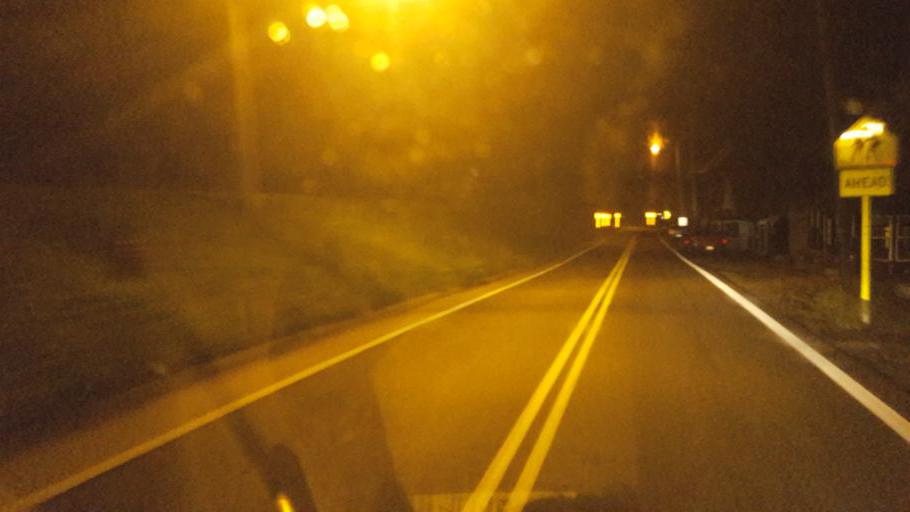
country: US
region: Ohio
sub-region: Holmes County
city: Millersburg
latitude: 40.5581
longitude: -81.9119
